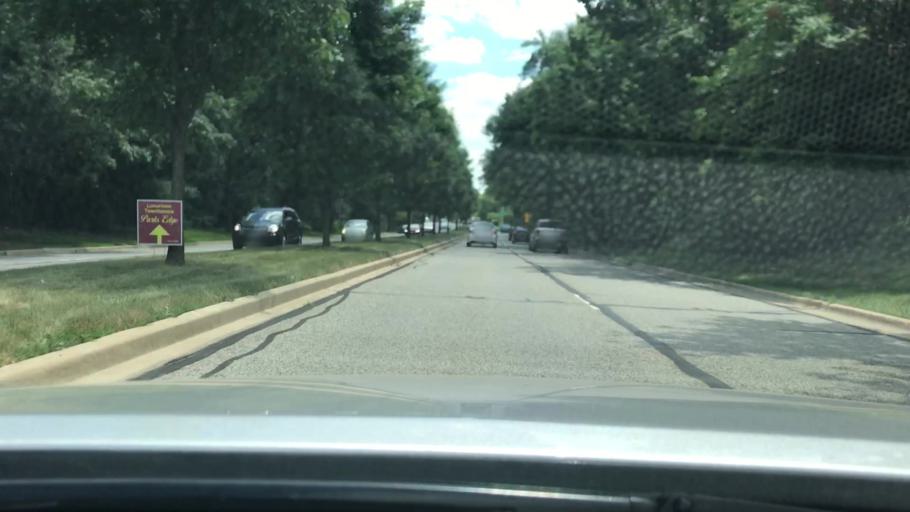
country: US
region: Illinois
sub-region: DuPage County
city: Naperville
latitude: 41.7948
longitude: -88.1190
